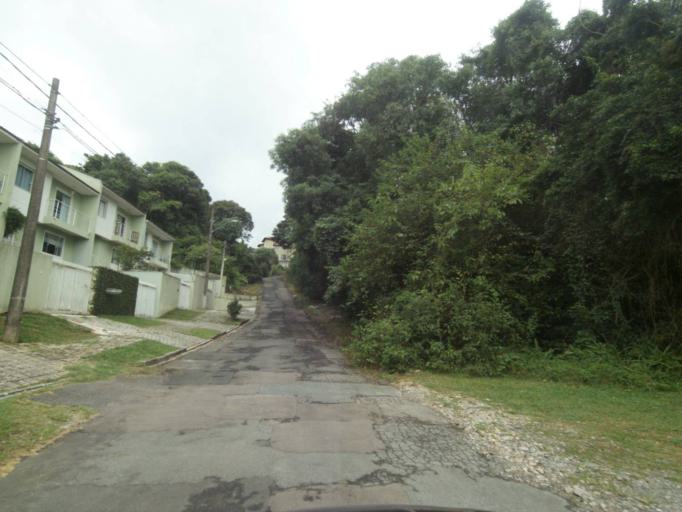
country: BR
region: Parana
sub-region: Curitiba
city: Curitiba
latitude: -25.4684
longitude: -49.3289
